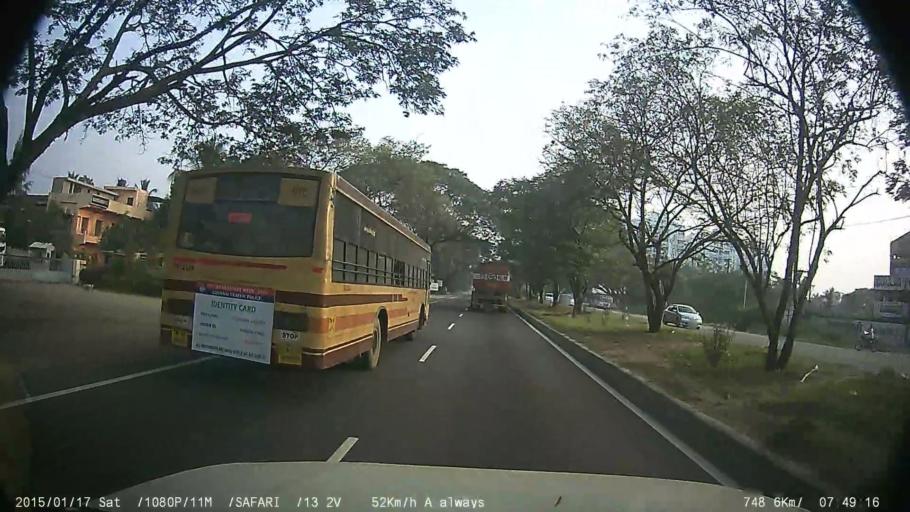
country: IN
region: Tamil Nadu
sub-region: Kancheepuram
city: Guduvancheri
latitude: 12.8561
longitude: 80.0692
